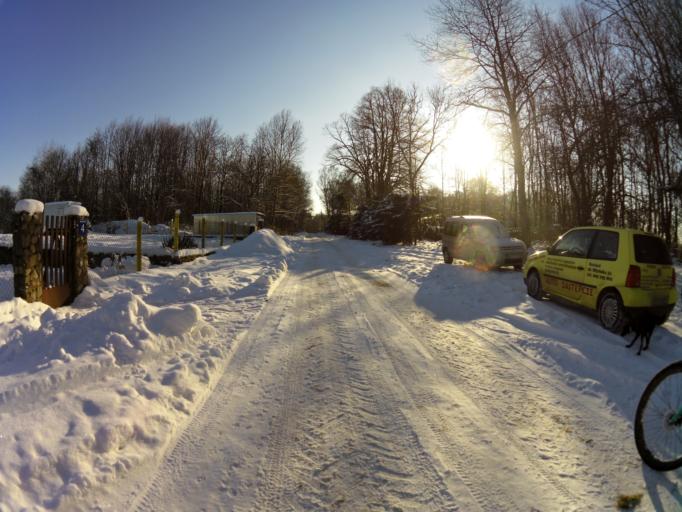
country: PL
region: West Pomeranian Voivodeship
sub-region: Powiat stargardzki
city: Dobrzany
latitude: 53.3737
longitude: 15.4836
